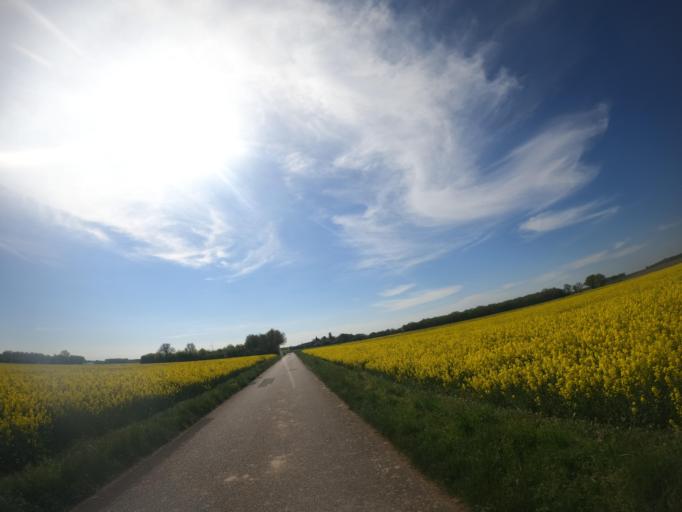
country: FR
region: Poitou-Charentes
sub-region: Departement des Deux-Sevres
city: Saint-Jean-de-Thouars
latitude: 46.9255
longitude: -0.2091
